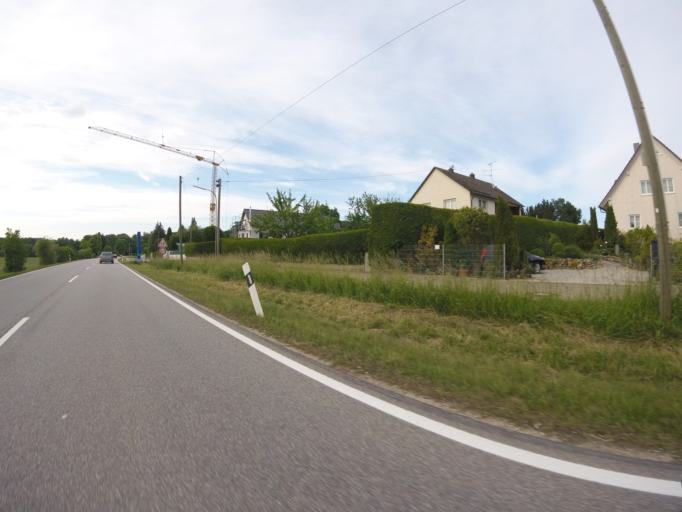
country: DE
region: Bavaria
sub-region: Upper Bavaria
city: Hettenshausen
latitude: 48.4988
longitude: 11.5112
